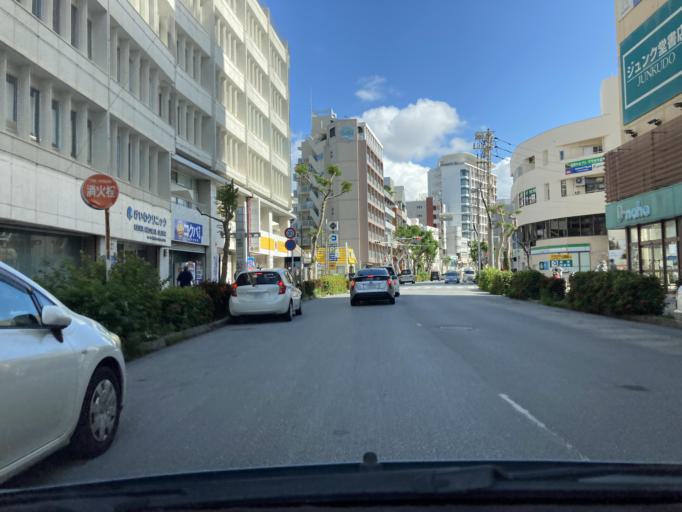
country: JP
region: Okinawa
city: Naha-shi
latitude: 26.2189
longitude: 127.6859
